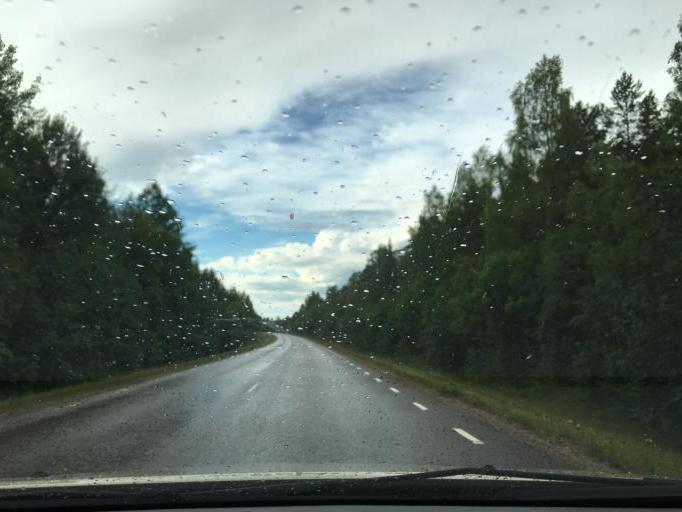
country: SE
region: Norrbotten
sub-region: Kalix Kommun
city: Toere
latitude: 66.0116
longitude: 22.8459
